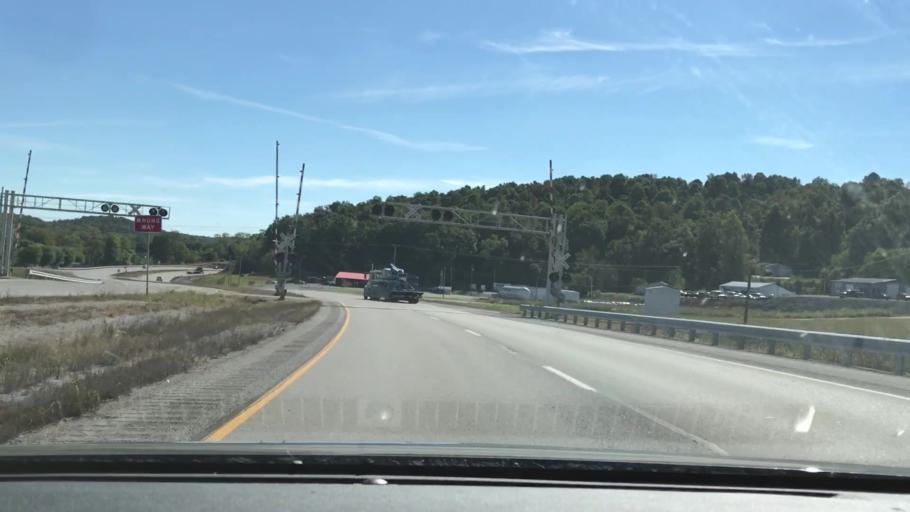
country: US
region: Kentucky
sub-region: Logan County
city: Russellville
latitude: 36.8353
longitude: -86.9157
